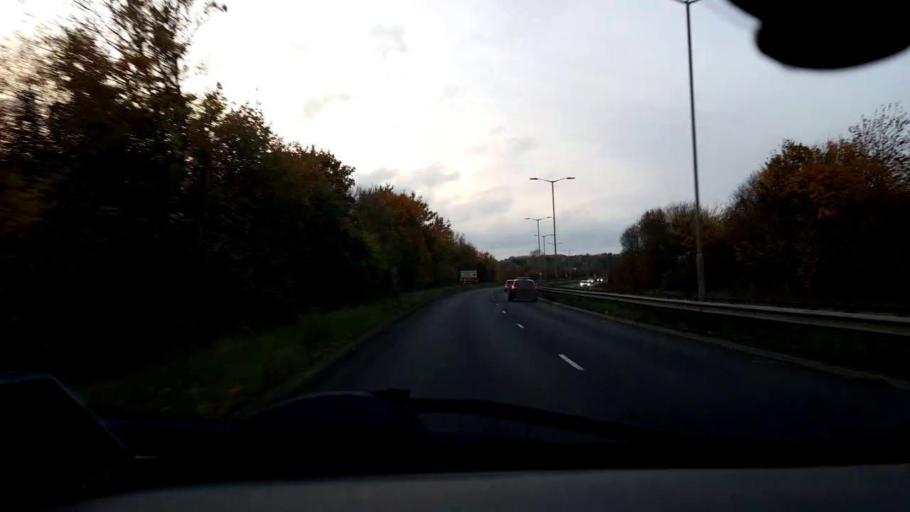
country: GB
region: England
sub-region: Norfolk
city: Thorpe Hamlet
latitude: 52.6086
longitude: 1.3155
